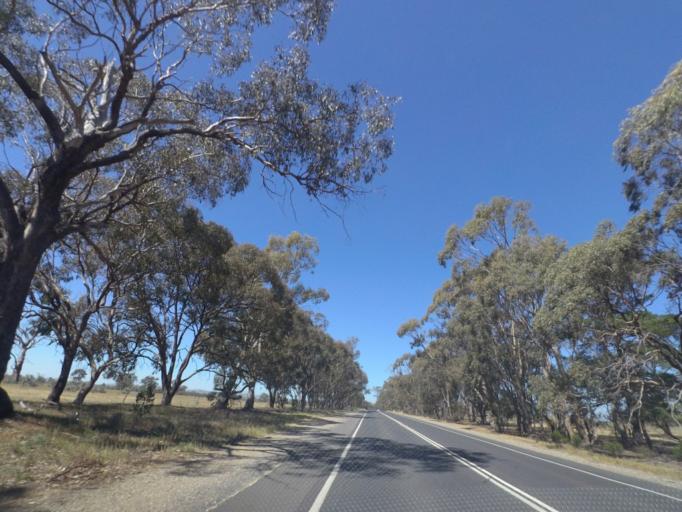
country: AU
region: Victoria
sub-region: Murrindindi
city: Kinglake West
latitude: -37.0295
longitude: 145.0764
